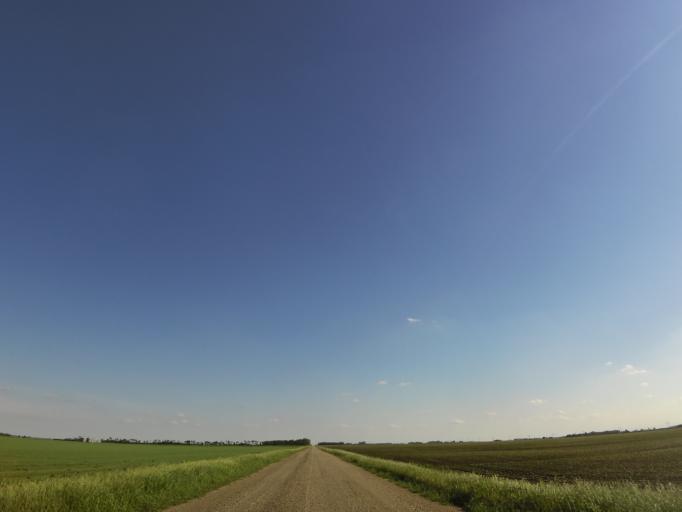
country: US
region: North Dakota
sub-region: Walsh County
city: Grafton
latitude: 48.4041
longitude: -97.2556
